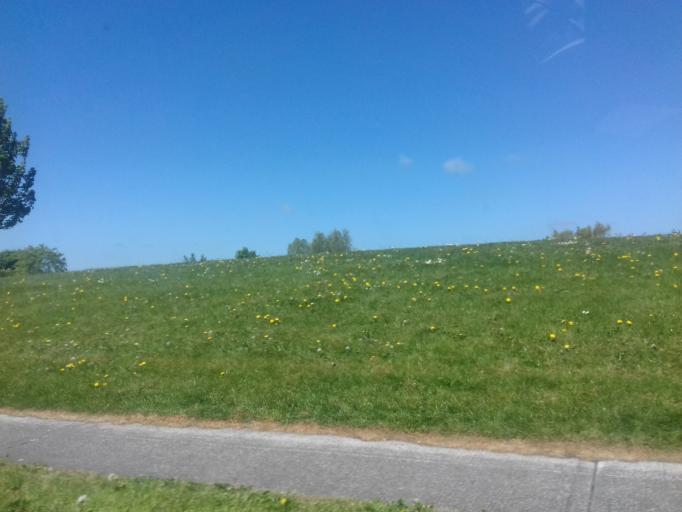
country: IE
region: Leinster
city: Cabra
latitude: 53.3736
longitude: -6.3133
